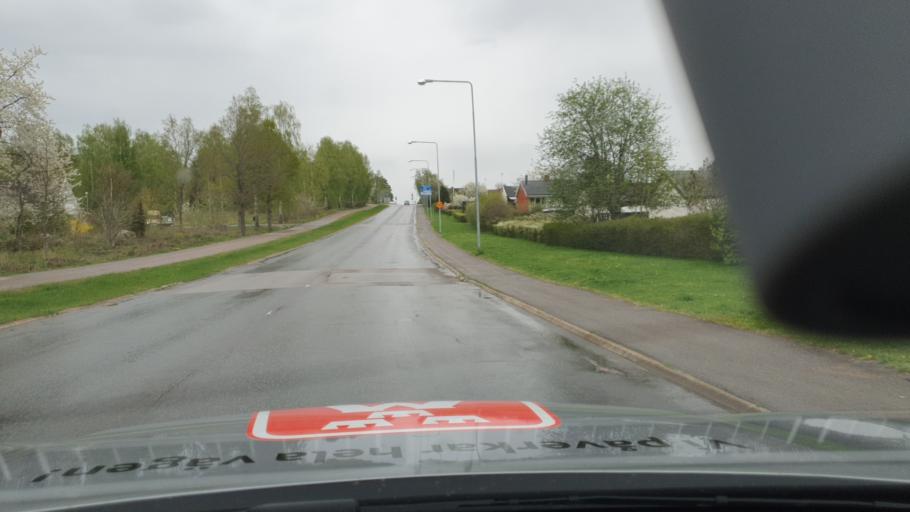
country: SE
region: Kalmar
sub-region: Vimmerby Kommun
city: Vimmerby
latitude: 57.6778
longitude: 15.8643
